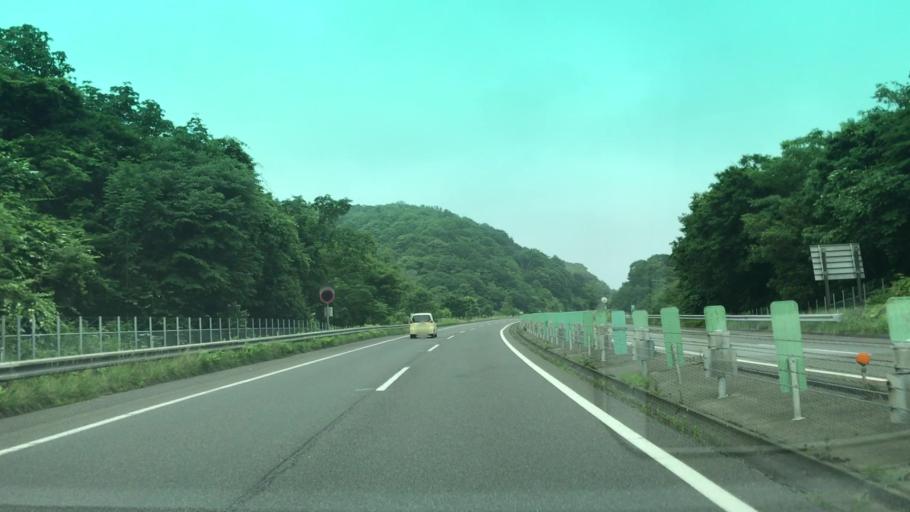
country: JP
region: Hokkaido
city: Shiraoi
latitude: 42.4835
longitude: 141.2241
